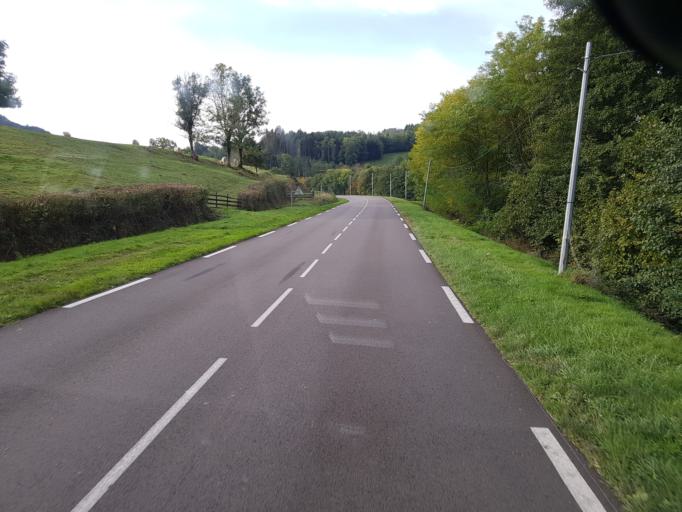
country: FR
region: Bourgogne
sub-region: Departement de Saone-et-Loire
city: La Clayette
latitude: 46.2769
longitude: 4.3746
